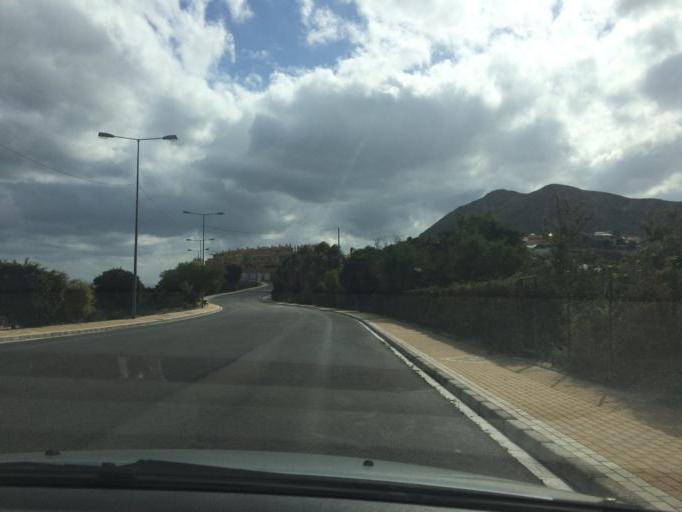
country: ES
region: Andalusia
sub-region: Provincia de Almeria
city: Vicar
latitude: 36.8375
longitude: -2.6137
